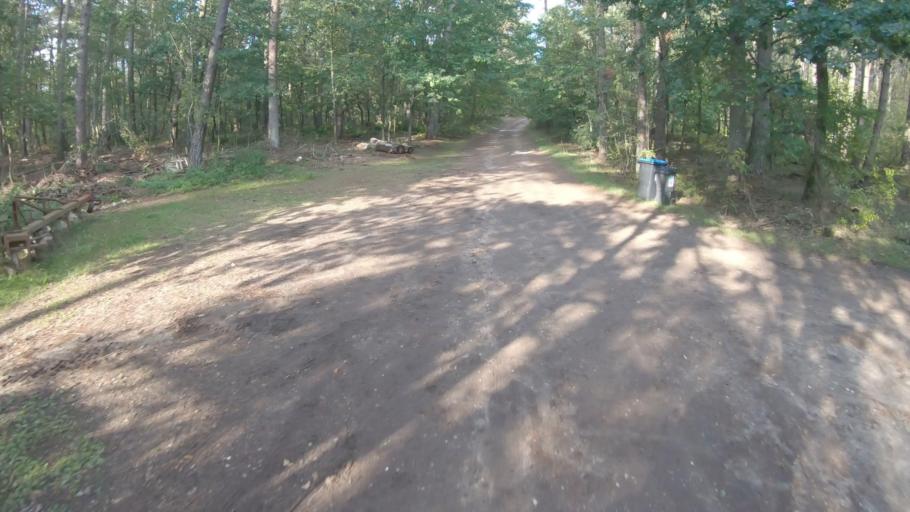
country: DE
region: Schleswig-Holstein
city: Rausdorf
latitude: 53.5935
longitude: 10.3366
